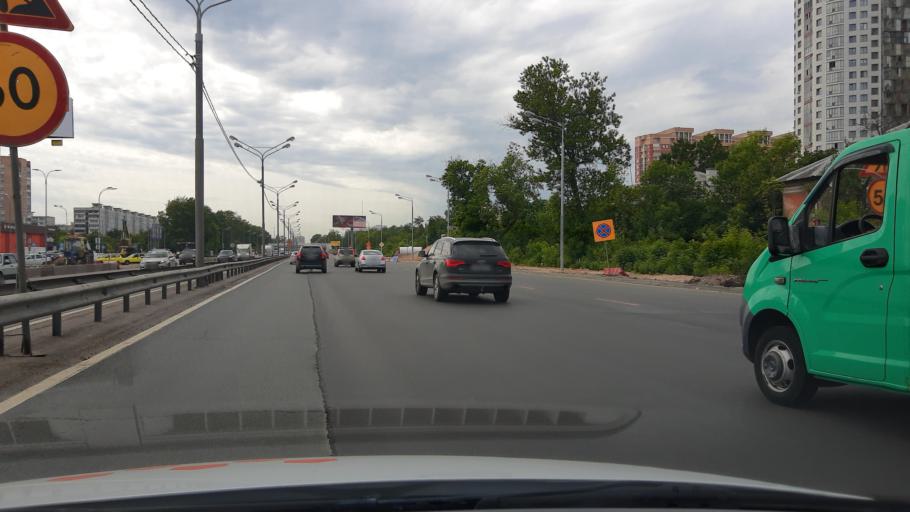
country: RU
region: Moskovskaya
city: Balashikha
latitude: 55.8001
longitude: 37.9885
